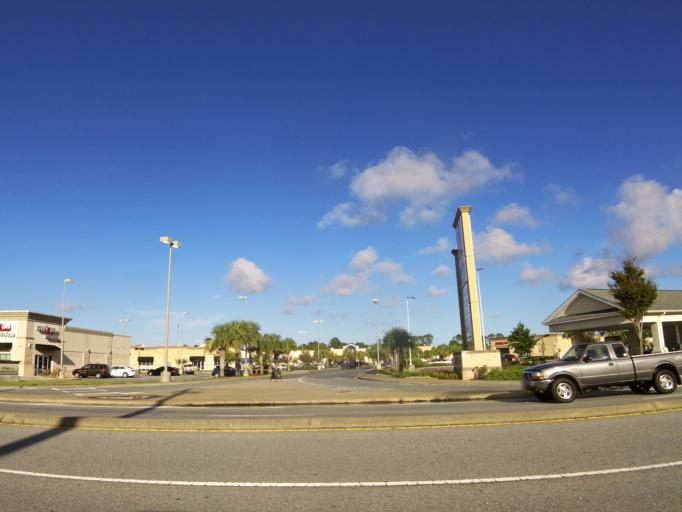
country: US
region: Georgia
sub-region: Glynn County
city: Country Club Estates
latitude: 31.2027
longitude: -81.4835
